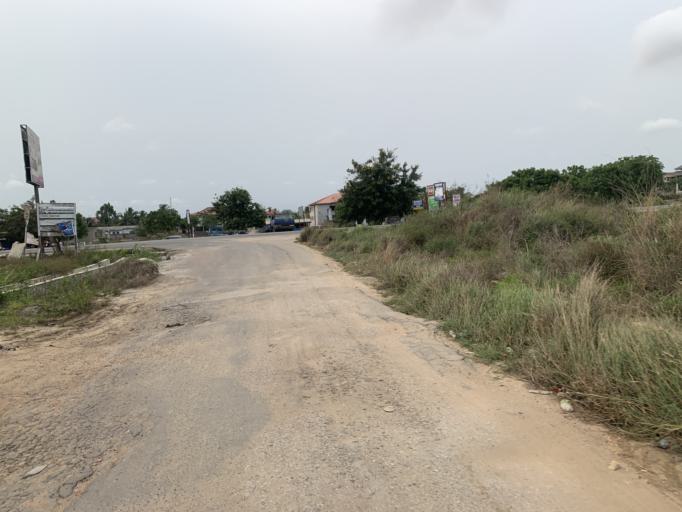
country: GH
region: Central
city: Winneba
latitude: 5.3892
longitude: -0.6351
